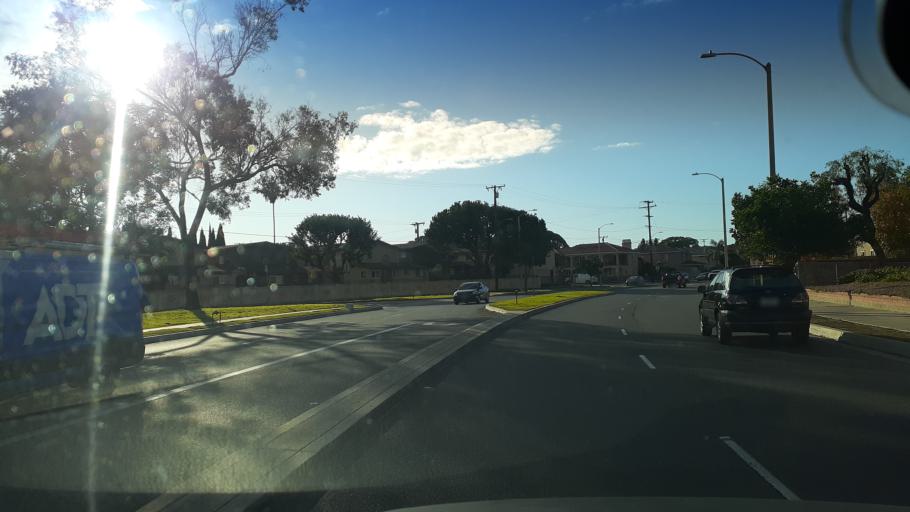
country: US
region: California
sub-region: Los Angeles County
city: West Carson
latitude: 33.8238
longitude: -118.3118
